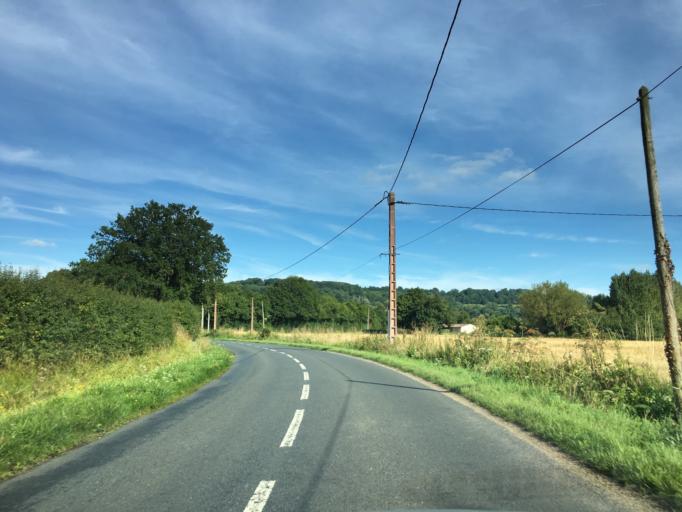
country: FR
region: Lower Normandy
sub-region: Departement du Calvados
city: Cambremer
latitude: 49.1598
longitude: -0.0110
